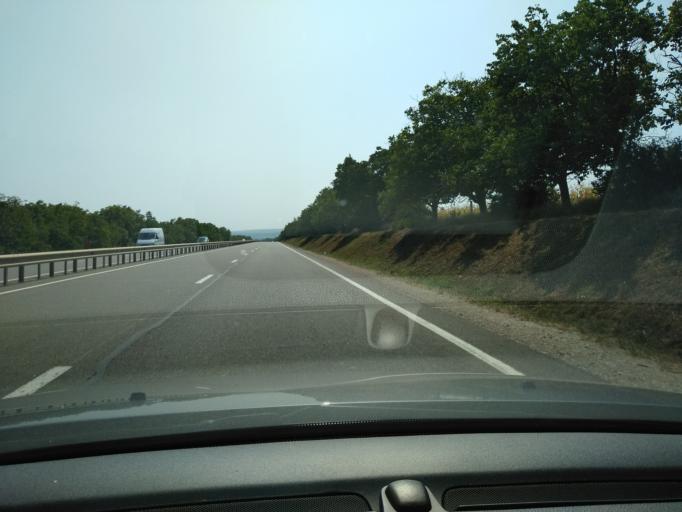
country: MD
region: Chisinau
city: Cricova
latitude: 47.2131
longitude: 28.7693
